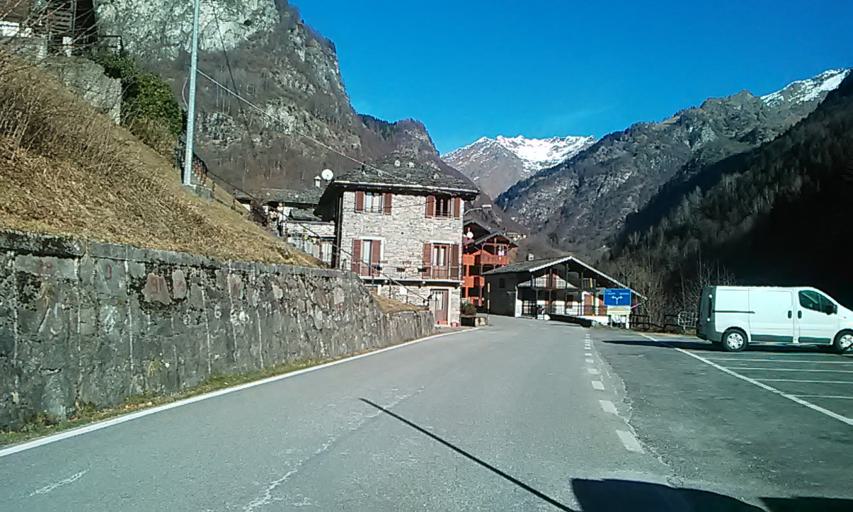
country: IT
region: Piedmont
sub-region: Provincia di Vercelli
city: Rimasco
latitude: 45.8563
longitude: 8.0631
